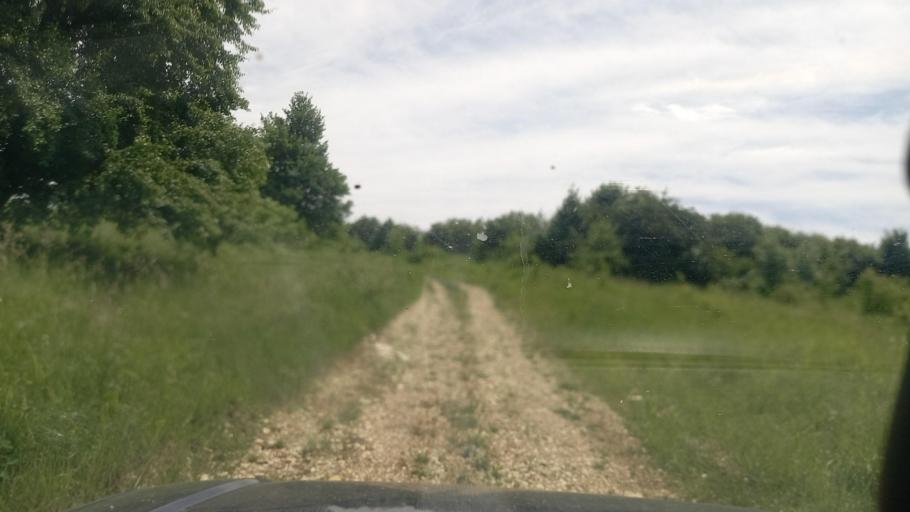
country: RU
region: Karachayevo-Cherkesiya
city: Pregradnaya
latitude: 44.0932
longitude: 41.1332
